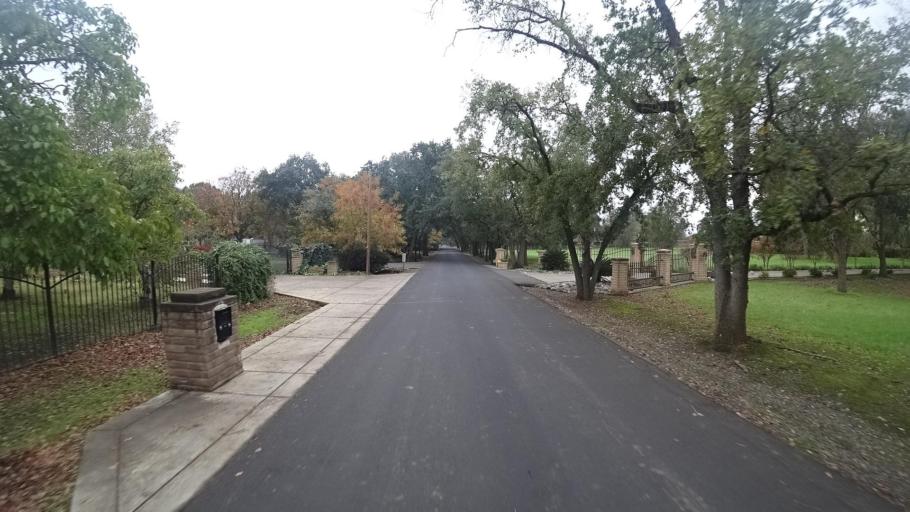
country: US
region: California
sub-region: Sacramento County
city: Wilton
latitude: 38.4353
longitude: -121.3115
